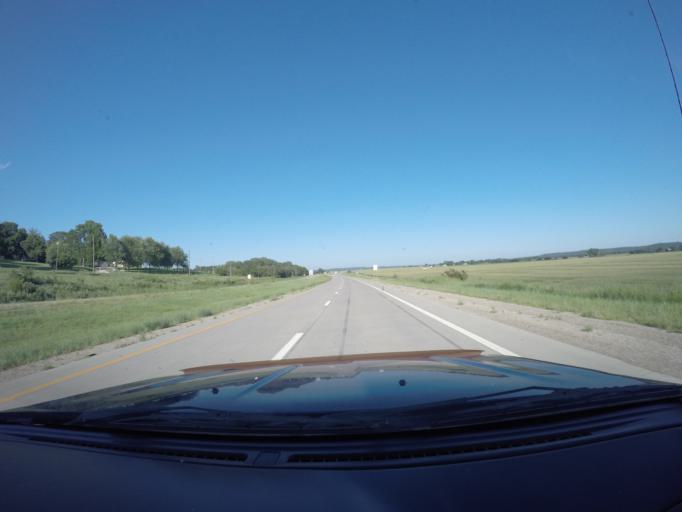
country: US
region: Kansas
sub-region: Shawnee County
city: Topeka
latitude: 39.0865
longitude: -95.4814
